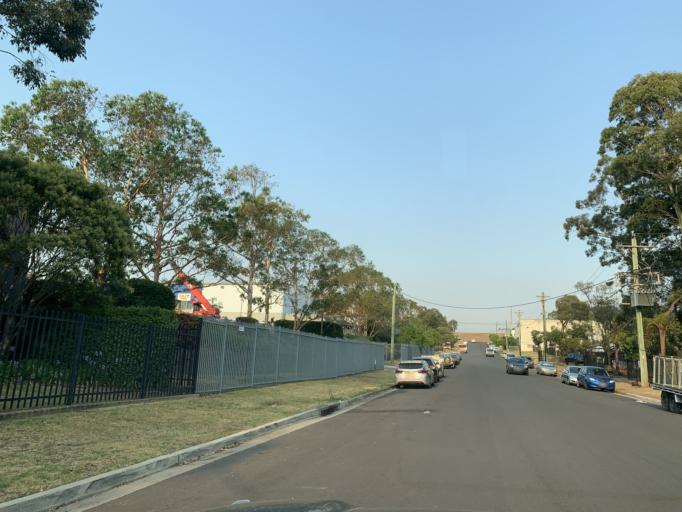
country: AU
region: New South Wales
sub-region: Fairfield
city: Horsley Park
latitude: -33.8393
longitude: 150.8837
